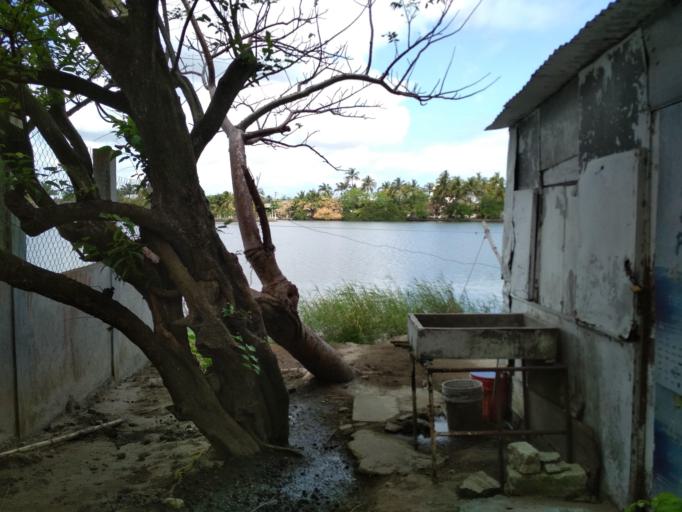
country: MX
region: Veracruz
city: Boca del Rio
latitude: 19.0974
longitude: -96.1098
